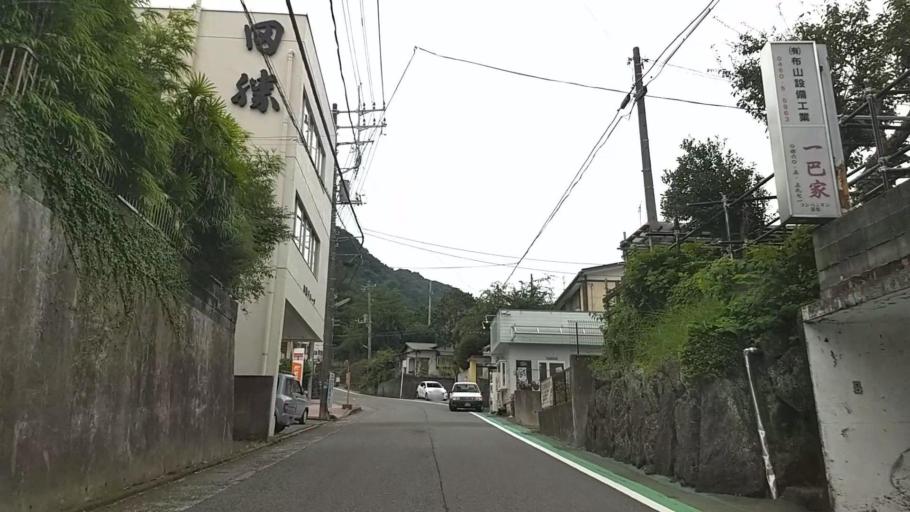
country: JP
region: Kanagawa
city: Odawara
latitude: 35.2308
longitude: 139.1068
